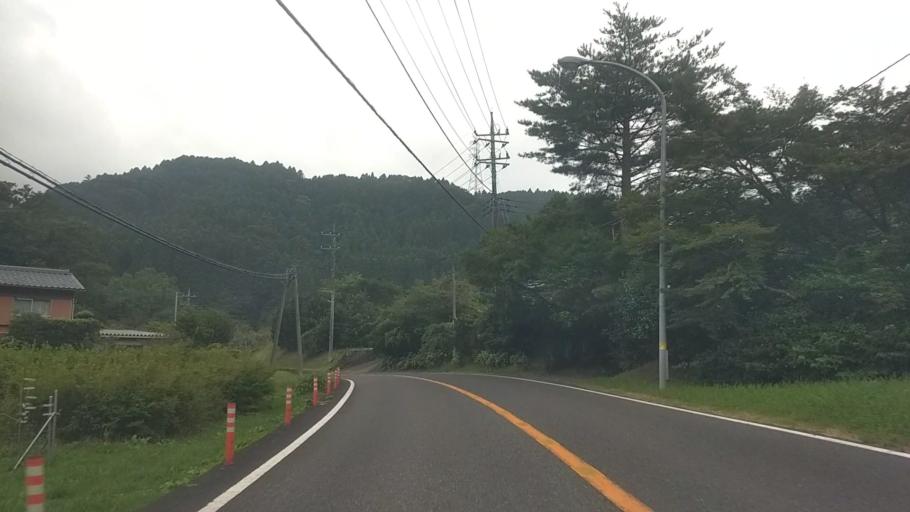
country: JP
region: Chiba
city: Kawaguchi
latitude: 35.2245
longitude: 140.0724
